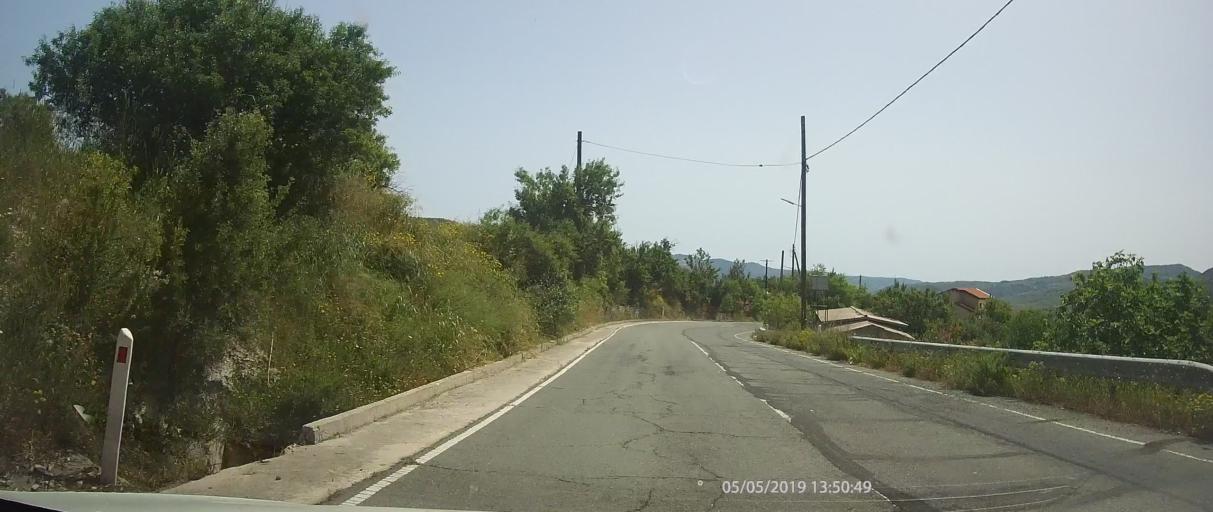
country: CY
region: Limassol
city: Pachna
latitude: 34.8396
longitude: 32.7362
